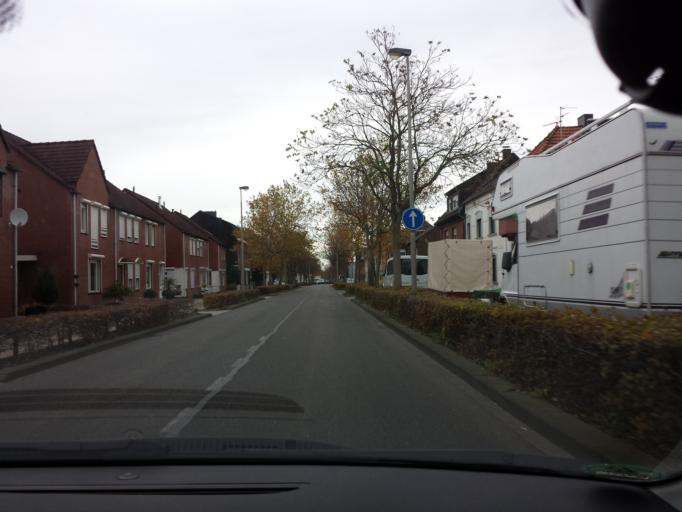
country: NL
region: Limburg
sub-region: Gemeente Kerkrade
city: Kerkrade
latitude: 50.8493
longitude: 6.0748
